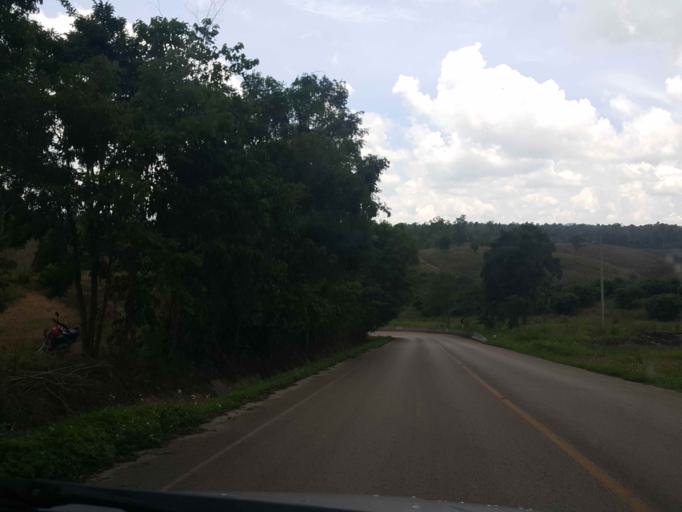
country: TH
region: Lampang
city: Ngao
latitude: 18.9431
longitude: 100.0770
